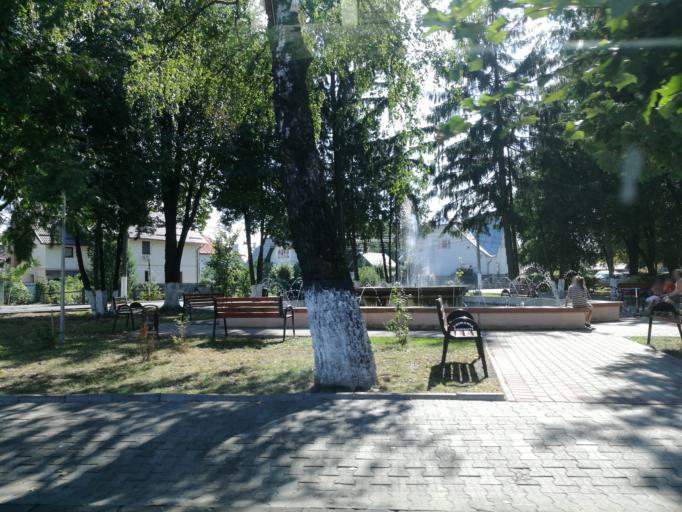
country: RO
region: Suceava
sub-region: Municipiul Suceava
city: Radauti
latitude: 47.8412
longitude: 25.9237
